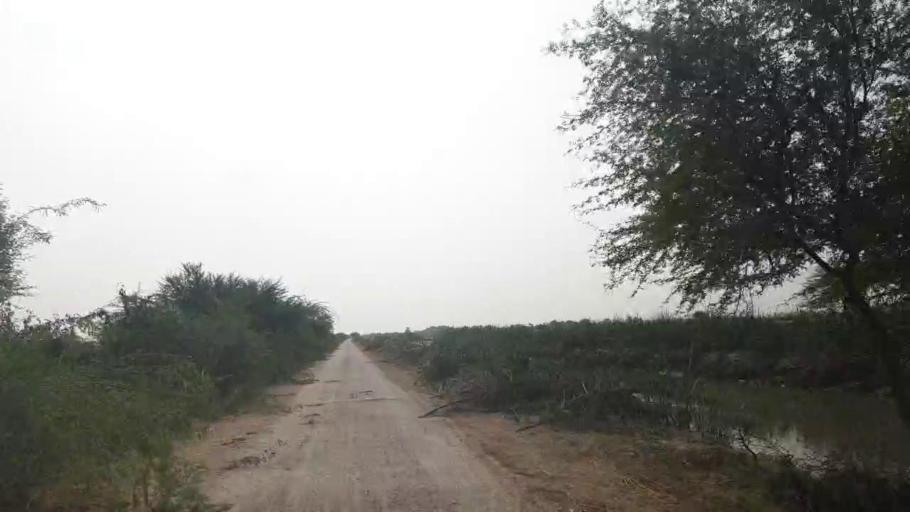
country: PK
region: Sindh
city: Badin
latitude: 24.7266
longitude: 68.7347
